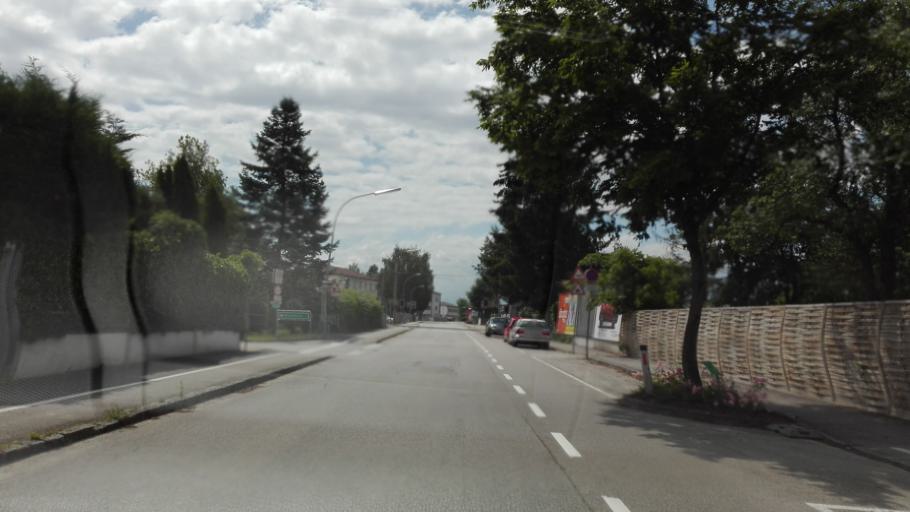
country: AT
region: Upper Austria
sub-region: Politischer Bezirk Perg
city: Perg
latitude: 48.2441
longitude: 14.6355
